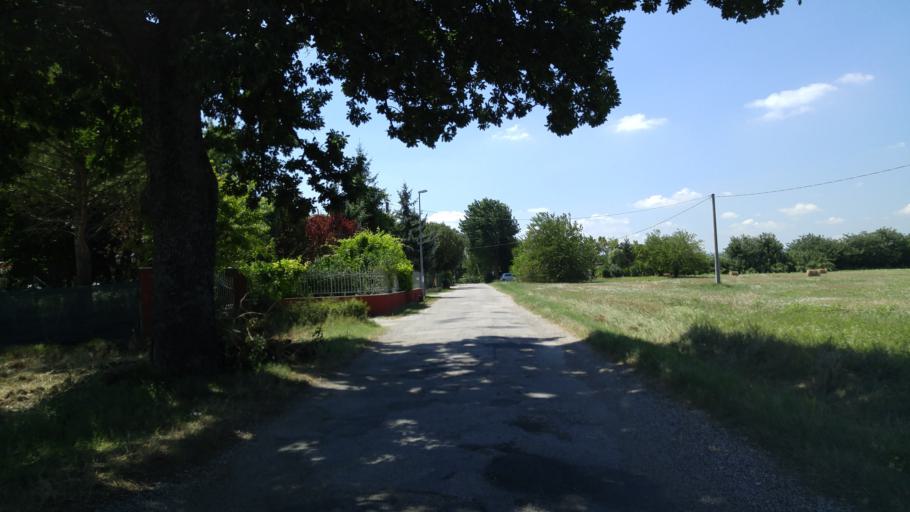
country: IT
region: The Marches
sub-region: Provincia di Pesaro e Urbino
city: Cuccurano
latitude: 43.7960
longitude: 12.9690
